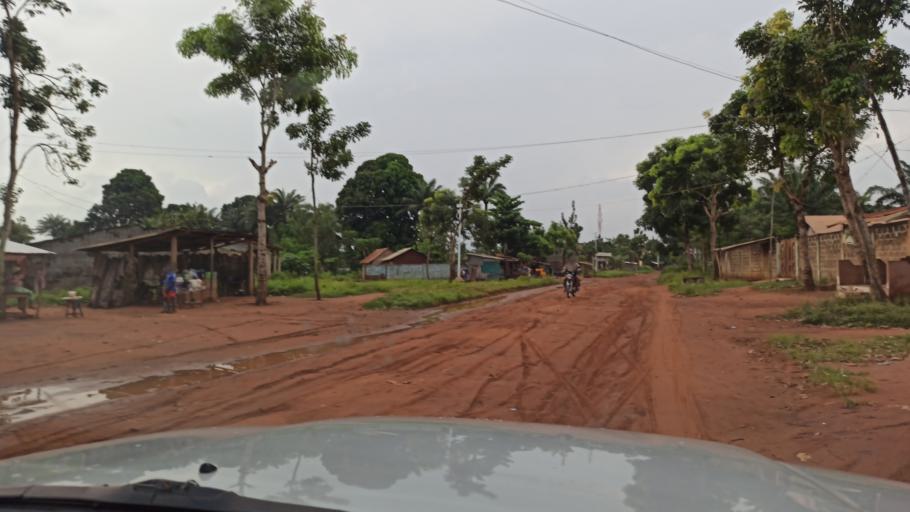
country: BJ
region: Queme
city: Porto-Novo
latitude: 6.4871
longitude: 2.6681
